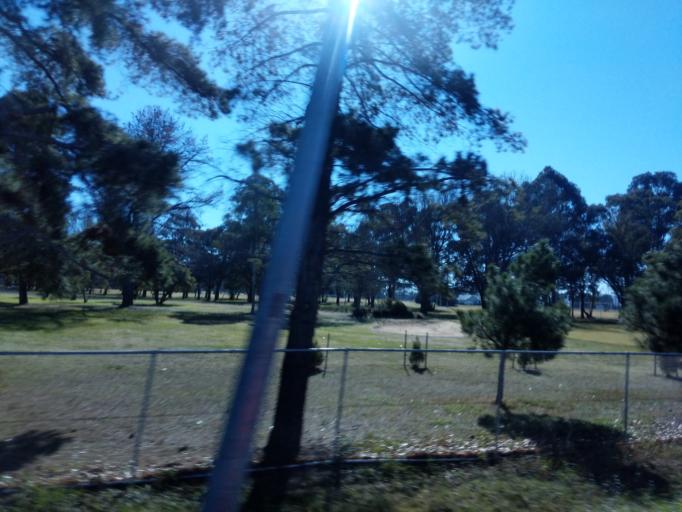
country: AU
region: Australian Capital Territory
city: Forrest
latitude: -35.3015
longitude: 149.1727
